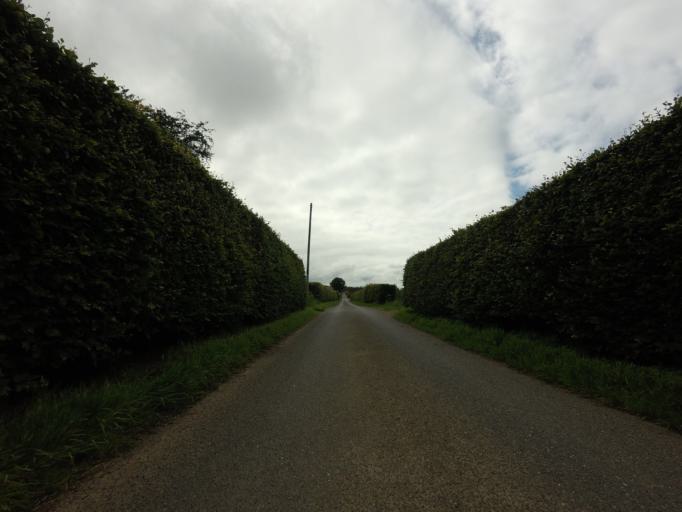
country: GB
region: Scotland
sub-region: Aberdeenshire
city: Turriff
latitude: 57.5432
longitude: -2.3009
